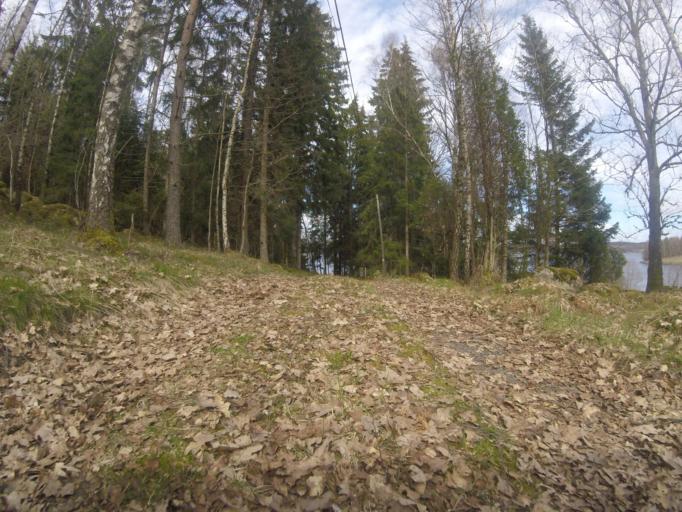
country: SE
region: Vaestra Goetaland
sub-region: Alingsas Kommun
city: Ingared
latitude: 57.8703
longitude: 12.5148
